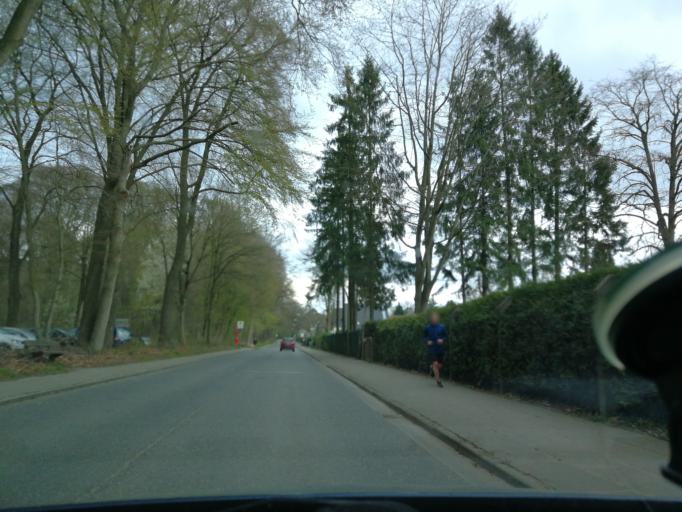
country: DE
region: Hamburg
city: Harburg
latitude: 53.4573
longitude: 9.9354
